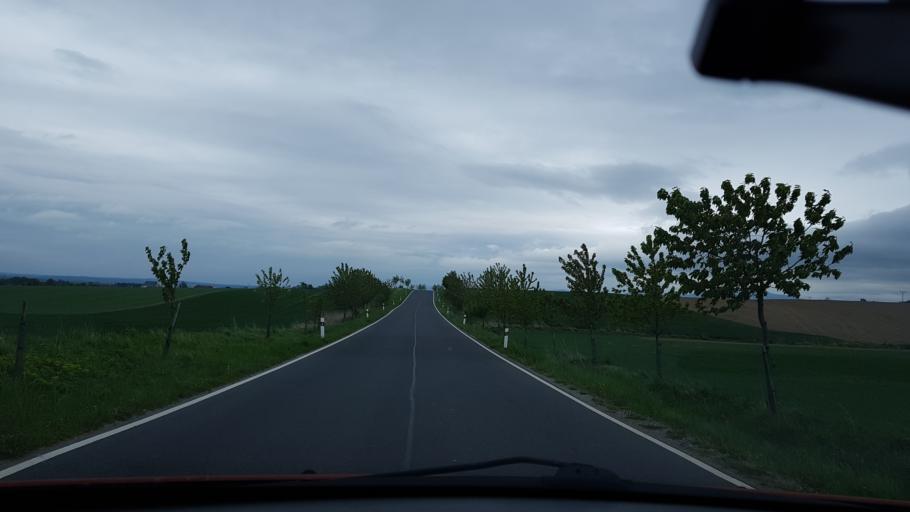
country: CZ
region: Olomoucky
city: Javornik
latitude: 50.4135
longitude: 16.9796
